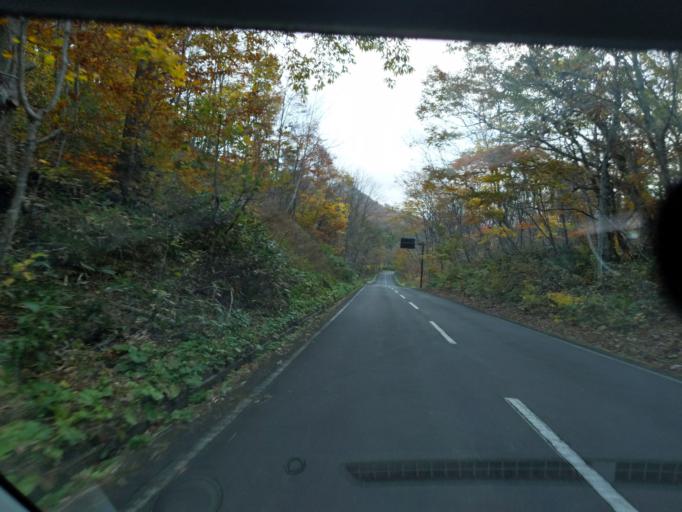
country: JP
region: Iwate
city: Mizusawa
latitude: 39.1123
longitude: 140.8794
